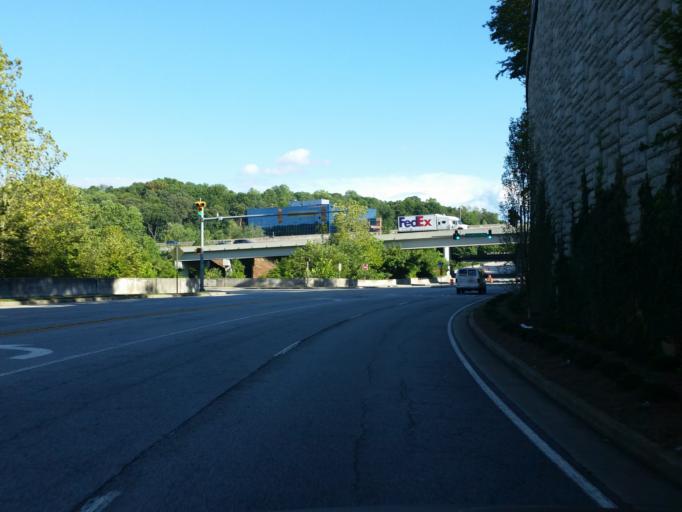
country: US
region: Georgia
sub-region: Cobb County
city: Vinings
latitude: 33.8940
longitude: -84.4585
